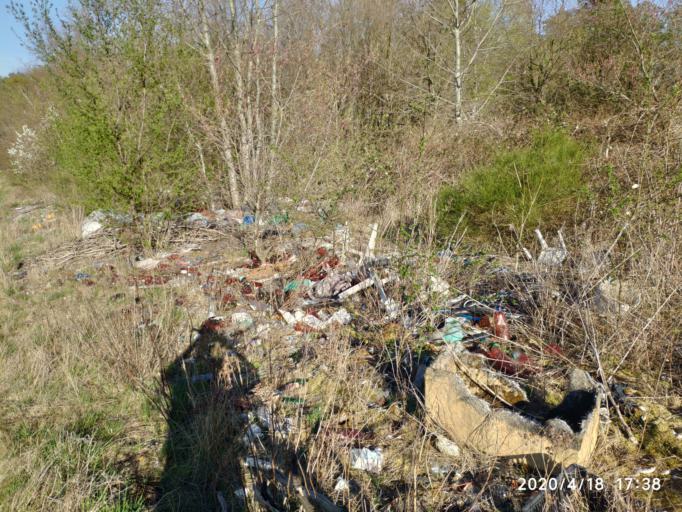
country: PL
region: Lubusz
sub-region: Powiat zielonogorski
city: Trzebiechow
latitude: 52.1003
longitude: 15.7199
